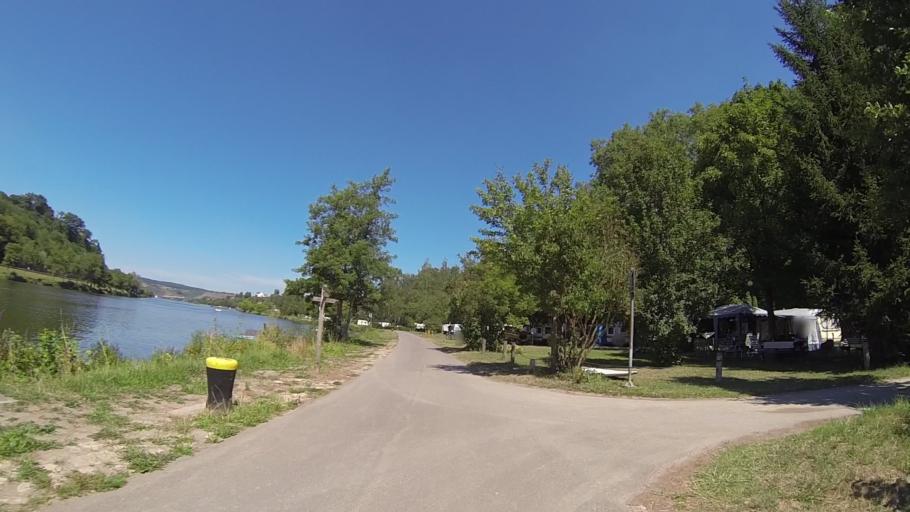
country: DE
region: Rheinland-Pfalz
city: Palzem
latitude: 49.5574
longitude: 6.3832
